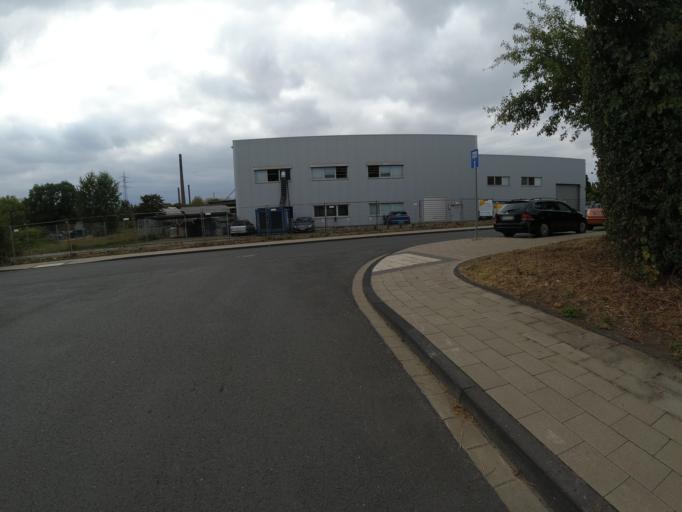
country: DE
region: North Rhine-Westphalia
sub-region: Regierungsbezirk Dusseldorf
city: Hochfeld
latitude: 51.4424
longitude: 6.7029
